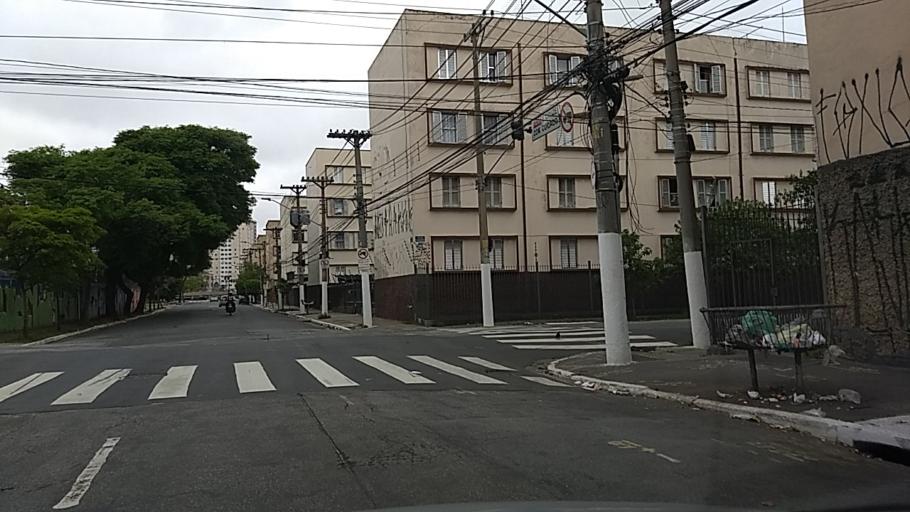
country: BR
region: Sao Paulo
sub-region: Sao Paulo
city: Sao Paulo
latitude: -23.5567
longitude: -46.6247
